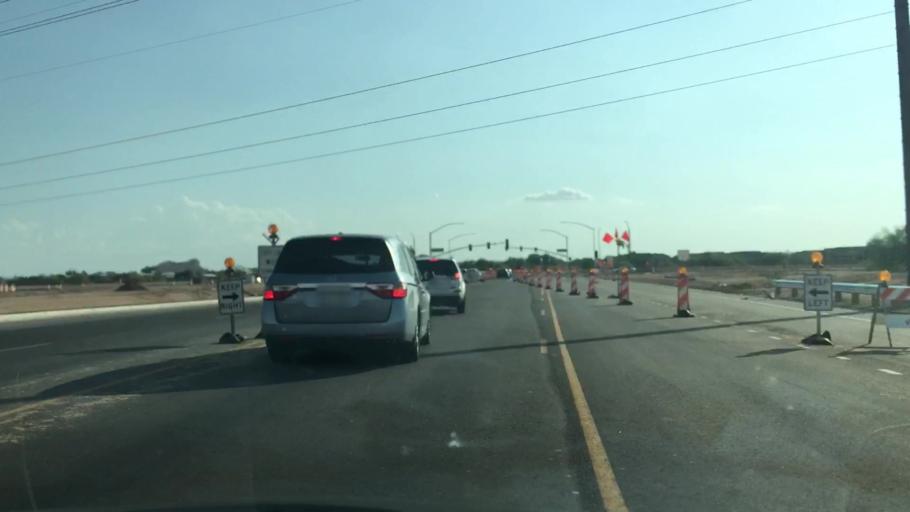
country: US
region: Arizona
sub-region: Pinal County
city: San Tan Valley
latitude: 33.1476
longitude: -111.5484
